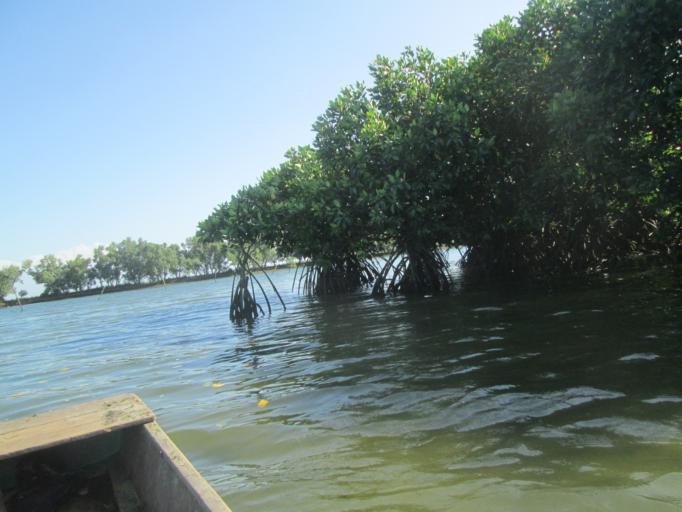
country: PH
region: Ilocos
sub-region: Province of Pangasinan
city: Pangapisan
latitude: 16.2443
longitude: 119.9310
